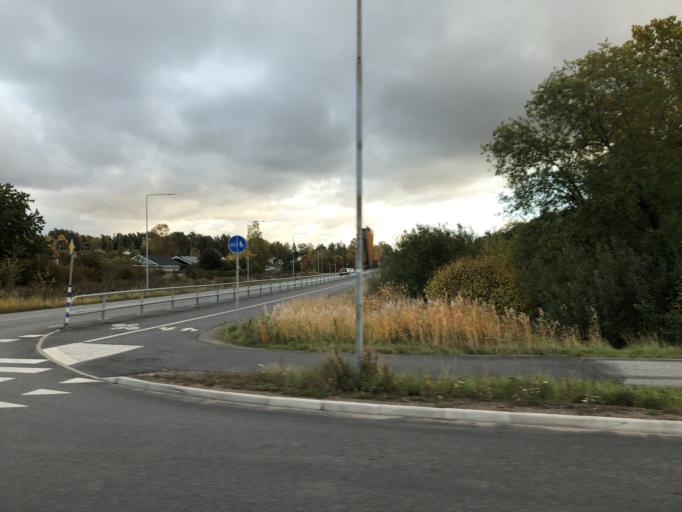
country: SE
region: Stockholm
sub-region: Jarfalla Kommun
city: Jakobsberg
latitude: 59.4230
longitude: 17.8041
